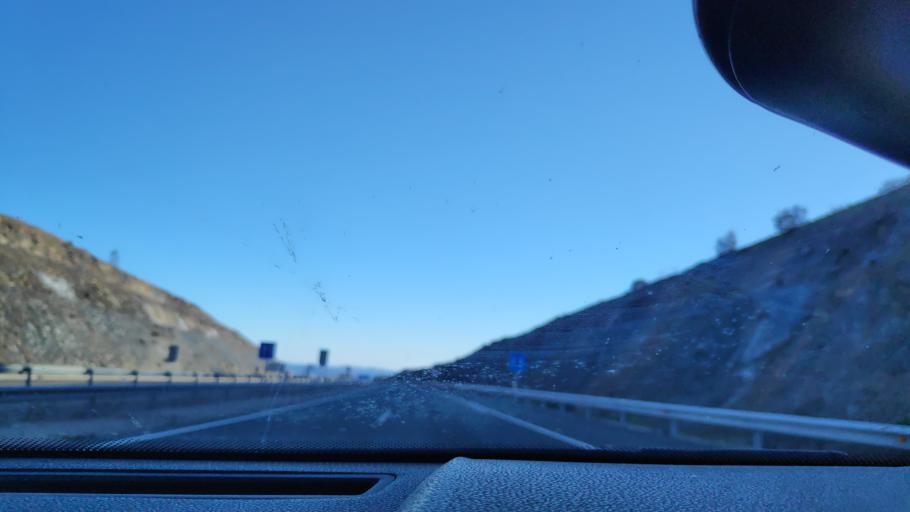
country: ES
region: Extremadura
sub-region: Provincia de Badajoz
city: Monesterio
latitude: 38.0791
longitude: -6.2587
